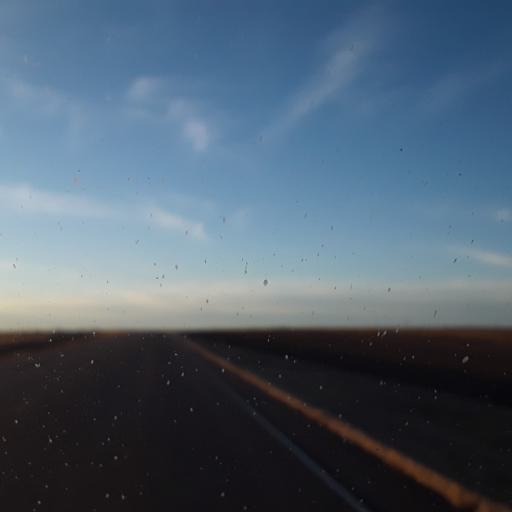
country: US
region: Colorado
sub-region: Cheyenne County
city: Cheyenne Wells
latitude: 38.8094
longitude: -102.4275
